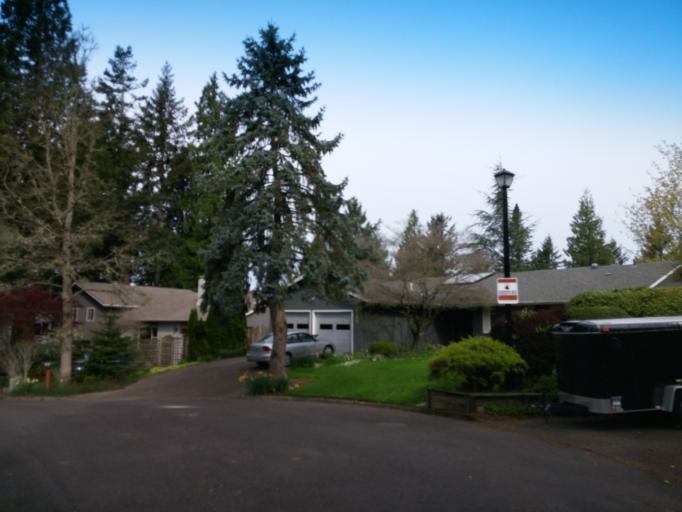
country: US
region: Oregon
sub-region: Washington County
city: Cedar Mill
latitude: 45.5399
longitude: -122.8018
